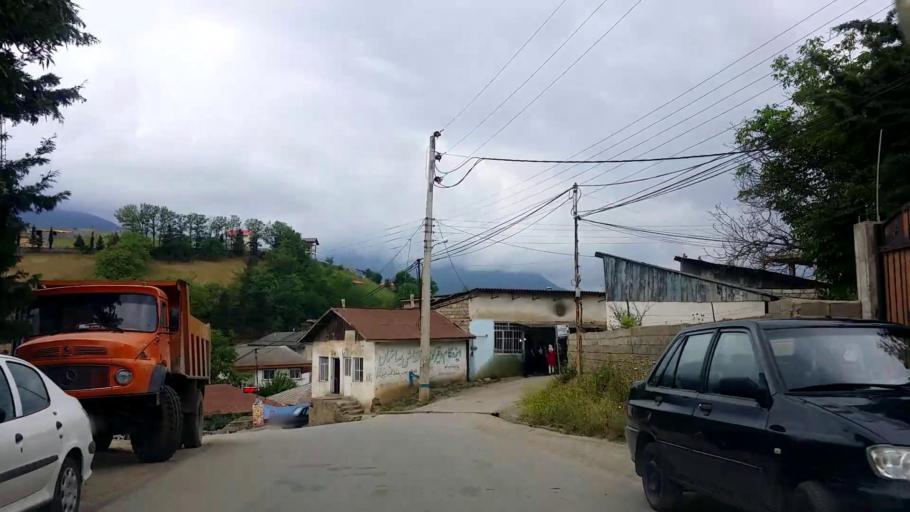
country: IR
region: Mazandaran
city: Chalus
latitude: 36.5137
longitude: 51.2569
